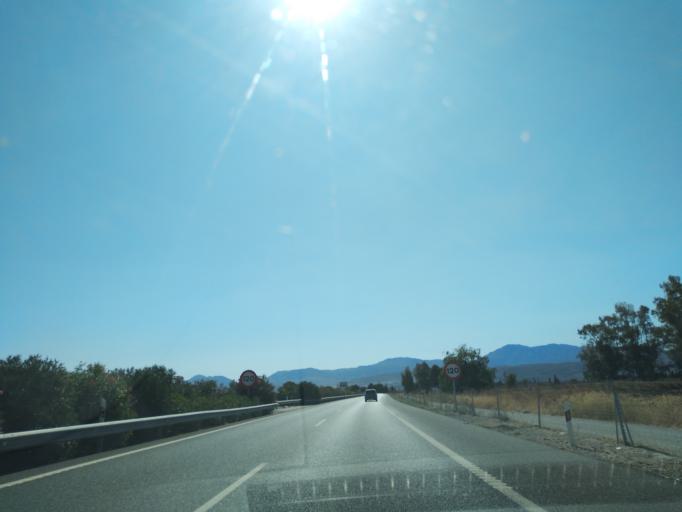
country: ES
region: Andalusia
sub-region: Provincia de Malaga
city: Mollina
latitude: 37.0919
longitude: -4.6267
